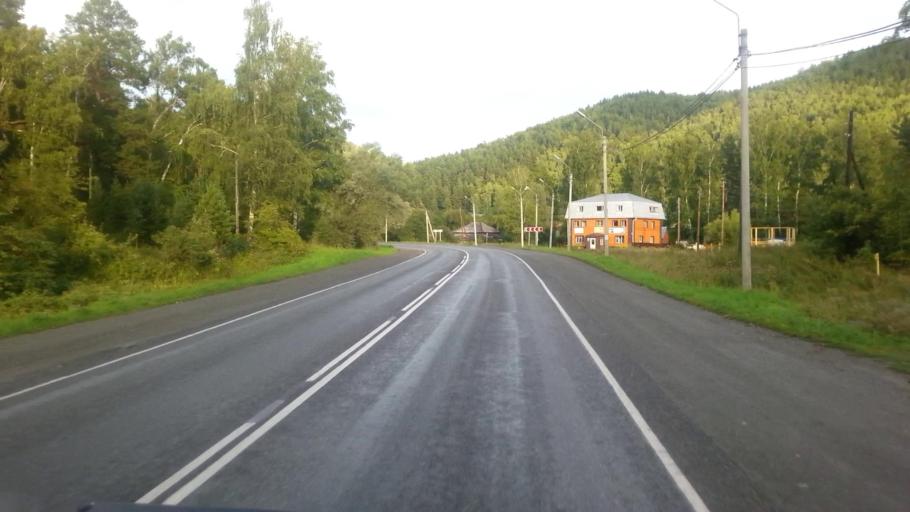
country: RU
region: Altay
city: Souzga
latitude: 51.8850
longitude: 85.8478
